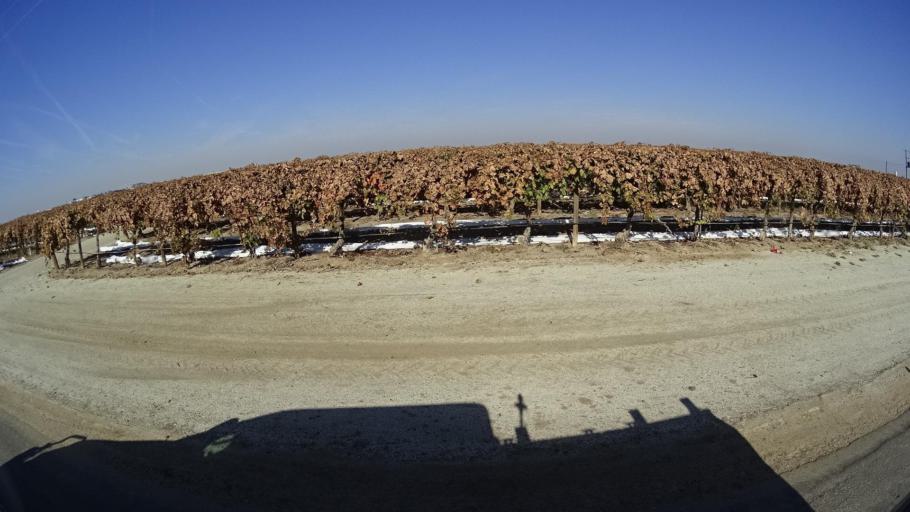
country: US
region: California
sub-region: Kern County
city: McFarland
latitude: 35.7034
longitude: -119.2158
